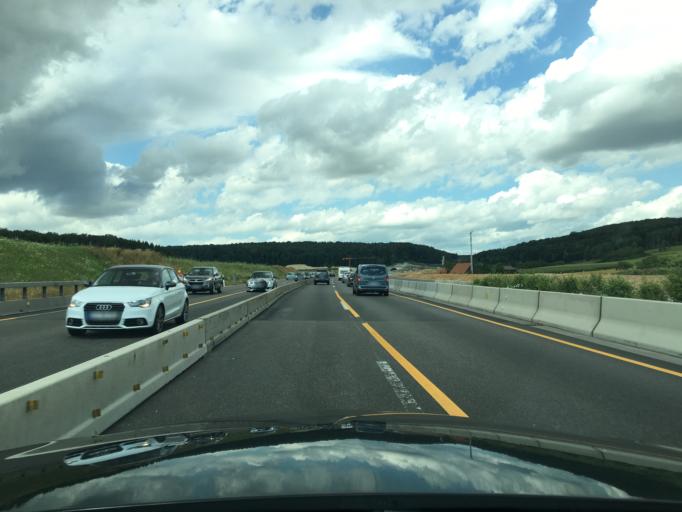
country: DE
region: Baden-Wuerttemberg
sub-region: Tuebingen Region
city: Lonsee
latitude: 48.4874
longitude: 9.8570
